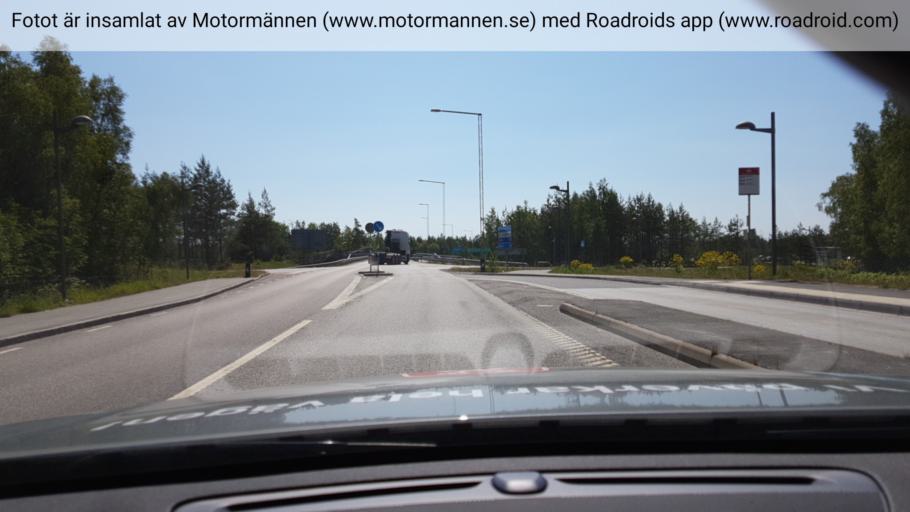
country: SE
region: Stockholm
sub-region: Norrtalje Kommun
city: Rimbo
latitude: 59.6376
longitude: 18.3337
